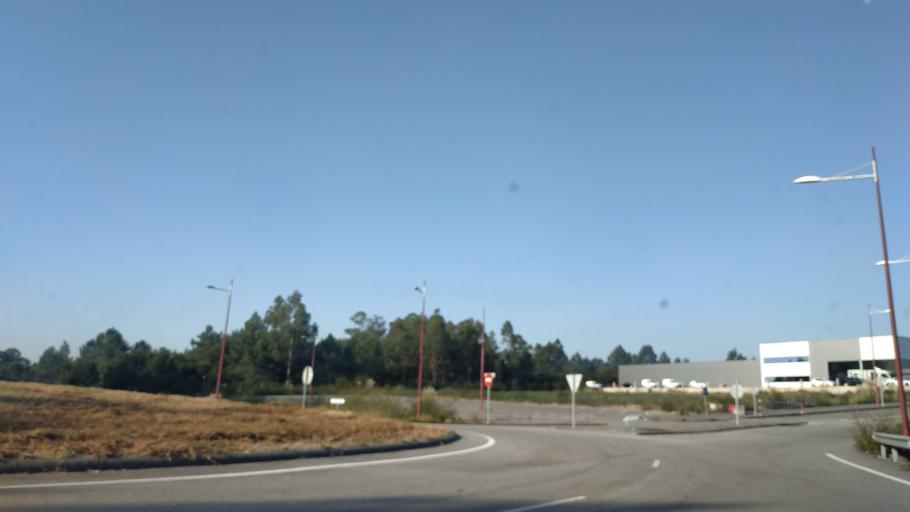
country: ES
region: Galicia
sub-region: Provincia da Coruna
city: Carballo
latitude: 43.2399
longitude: -8.6775
